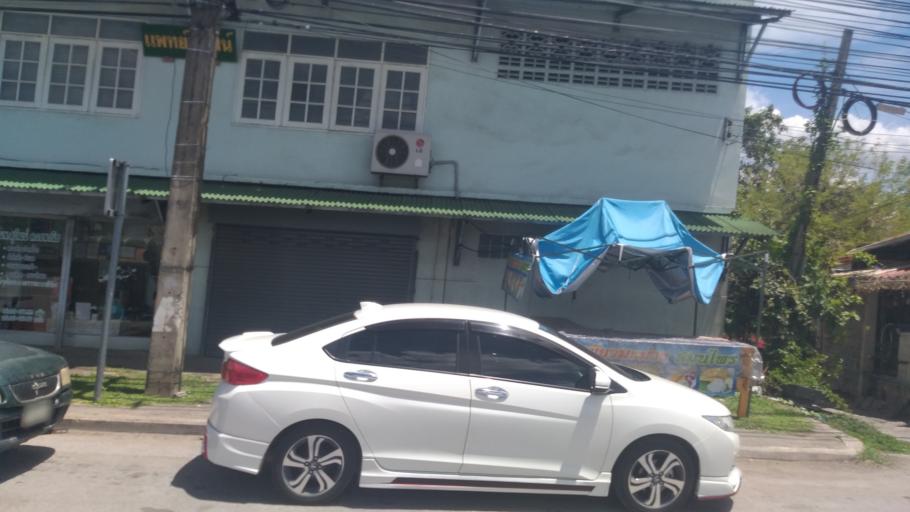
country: TH
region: Nakhon Nayok
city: Ban Na
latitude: 14.2620
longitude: 101.0681
